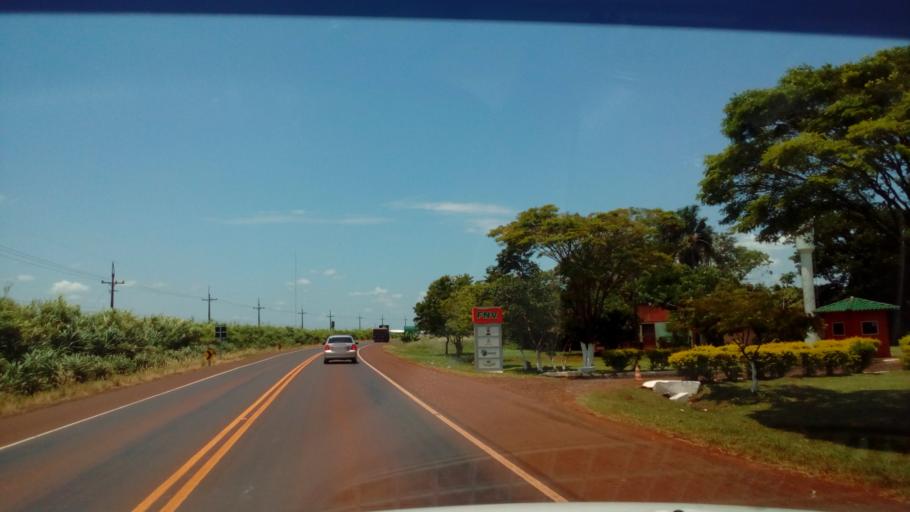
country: PY
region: Alto Parana
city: Santa Rita
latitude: -25.8693
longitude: -55.1175
